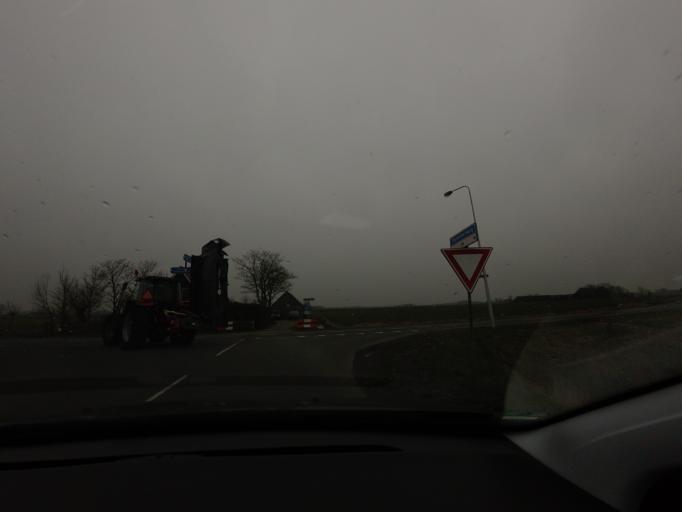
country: NL
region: Friesland
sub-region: Gemeente Franekeradeel
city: Franeker
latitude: 53.1720
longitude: 5.5486
